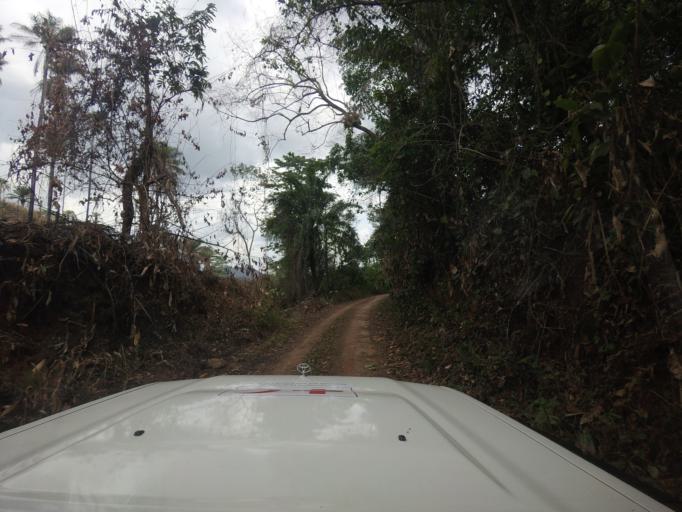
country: LR
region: Lofa
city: Voinjama
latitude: 8.3939
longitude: -9.6277
